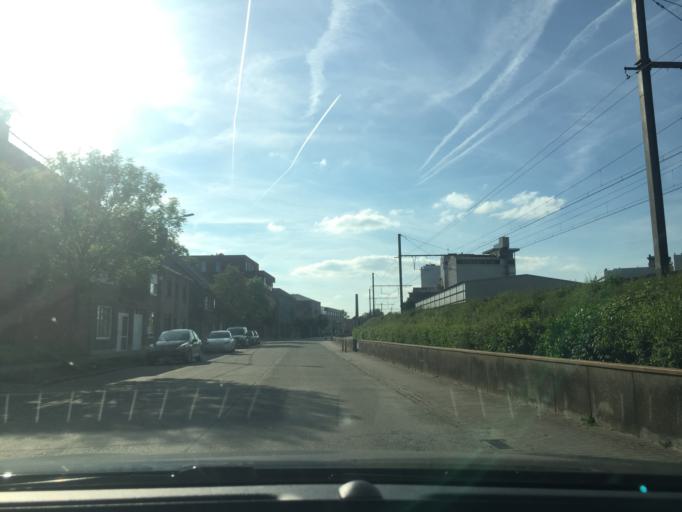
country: BE
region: Flanders
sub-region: Provincie West-Vlaanderen
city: Roeselare
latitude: 50.9410
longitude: 3.1389
